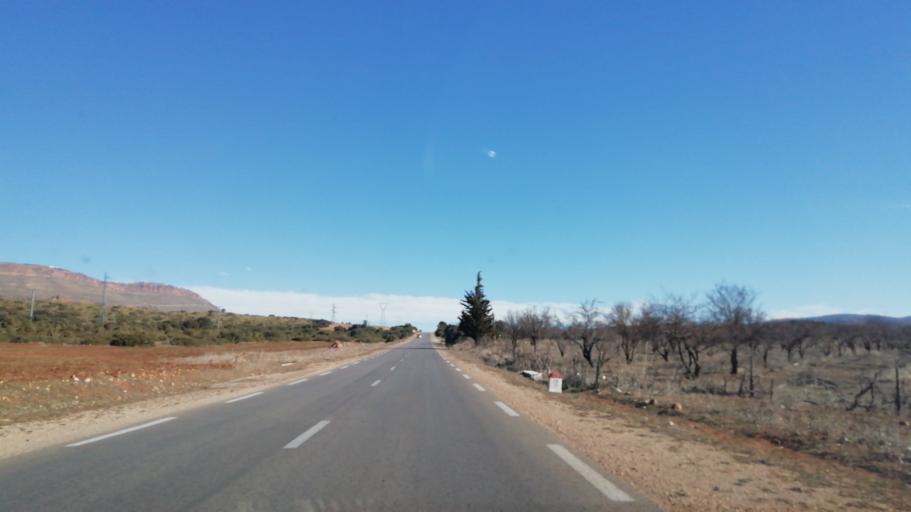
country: DZ
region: Tlemcen
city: Sebdou
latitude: 34.7096
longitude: -1.2127
